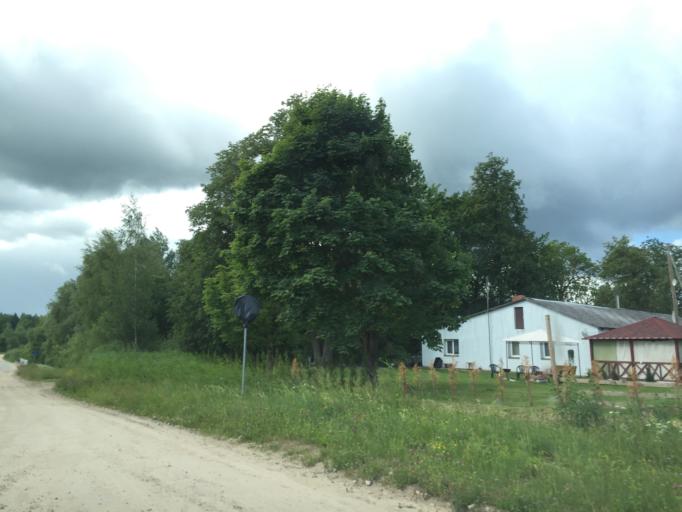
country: LV
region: Lecava
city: Iecava
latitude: 56.6241
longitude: 24.1853
